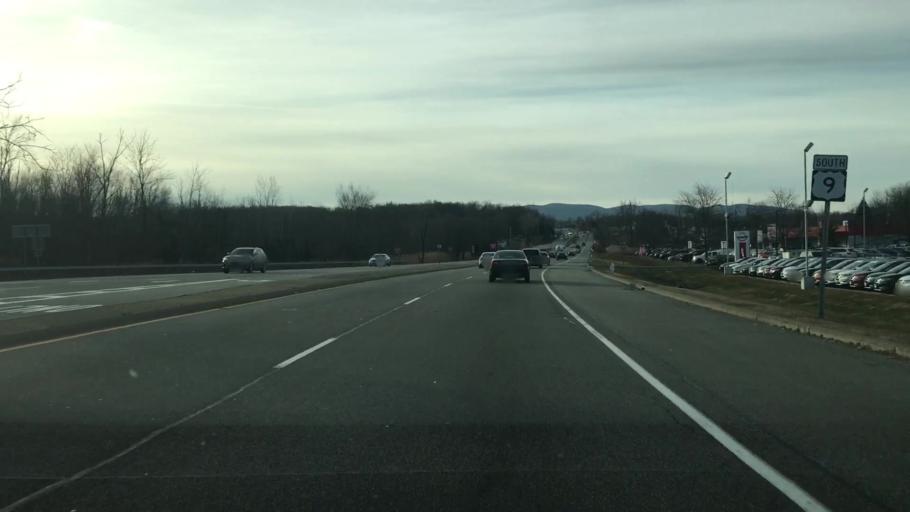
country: US
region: New York
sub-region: Dutchess County
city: Wappingers Falls
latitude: 41.5881
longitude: -73.9078
